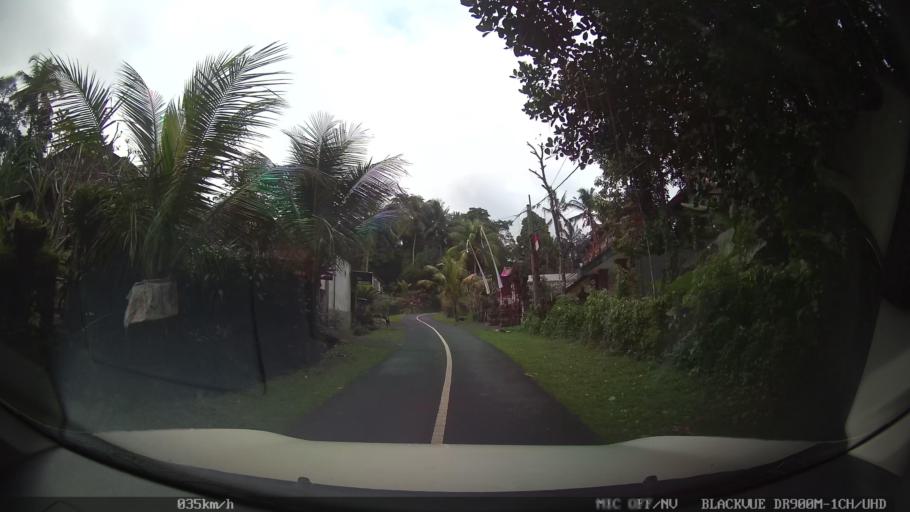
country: ID
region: Bali
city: Pegongan
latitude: -8.4773
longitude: 115.2308
